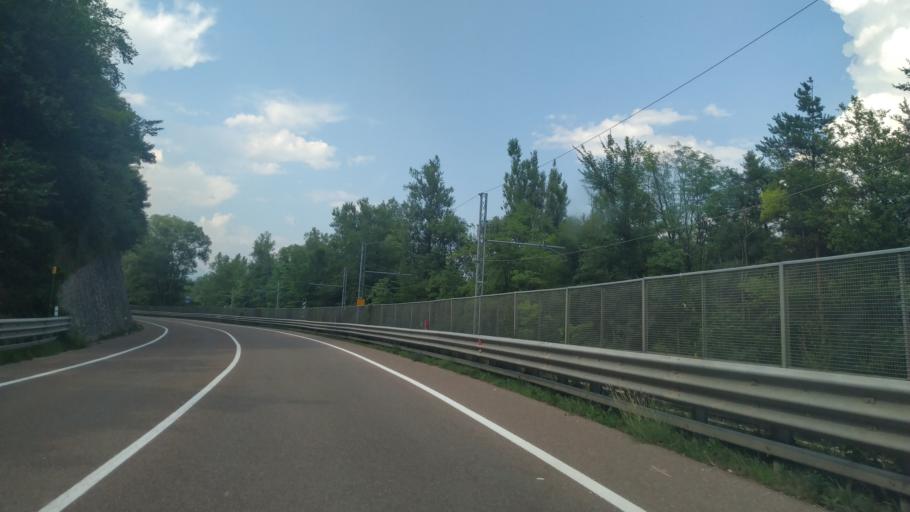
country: IT
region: Trentino-Alto Adige
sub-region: Provincia di Trento
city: Denno
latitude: 46.2564
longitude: 11.0586
